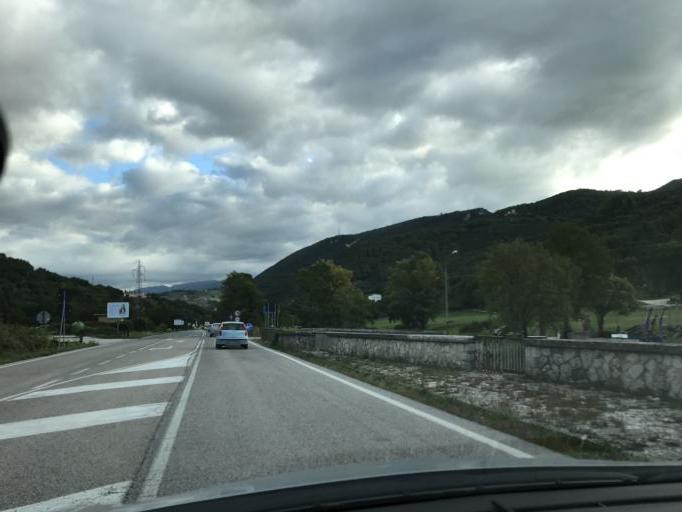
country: IT
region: Umbria
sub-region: Provincia di Perugia
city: Spoleto
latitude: 42.7164
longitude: 12.7245
